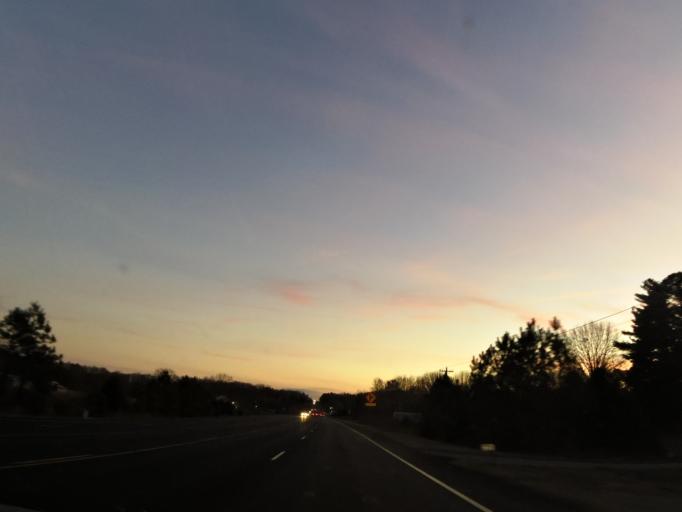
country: US
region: Georgia
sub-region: Whitfield County
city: Varnell
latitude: 34.9348
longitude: -84.9446
